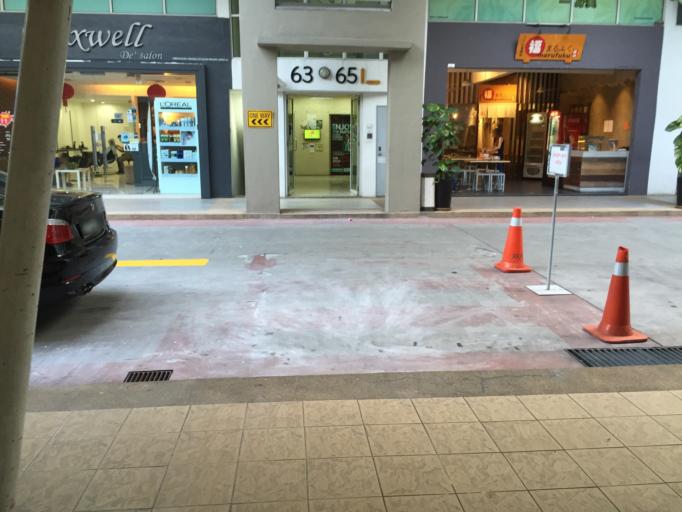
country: MY
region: Selangor
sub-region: Petaling
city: Petaling Jaya
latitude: 3.1176
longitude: 101.6355
